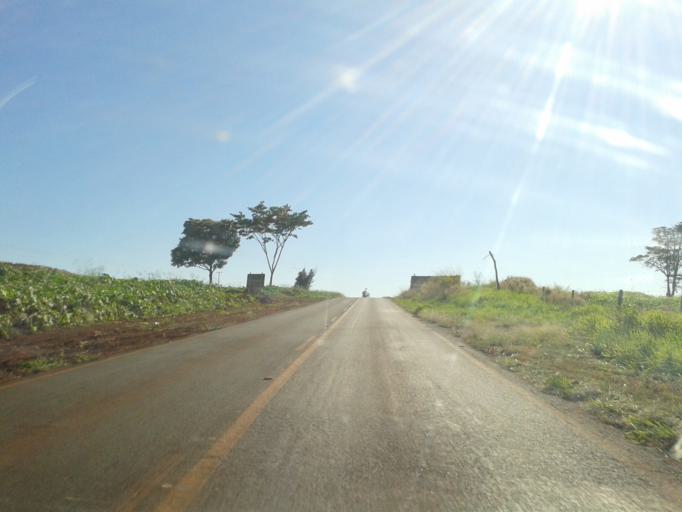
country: BR
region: Minas Gerais
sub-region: Capinopolis
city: Capinopolis
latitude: -18.6699
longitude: -49.5612
